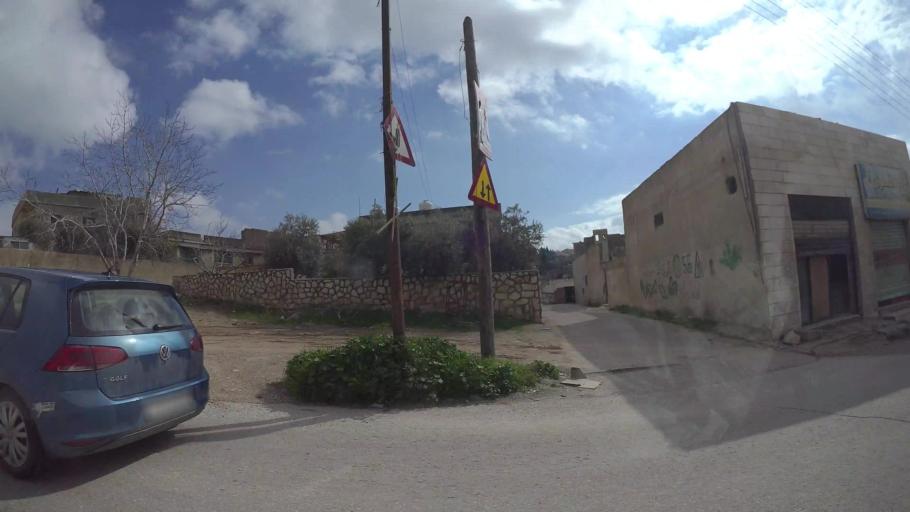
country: JO
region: Amman
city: Al Jubayhah
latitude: 32.0767
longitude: 35.8630
